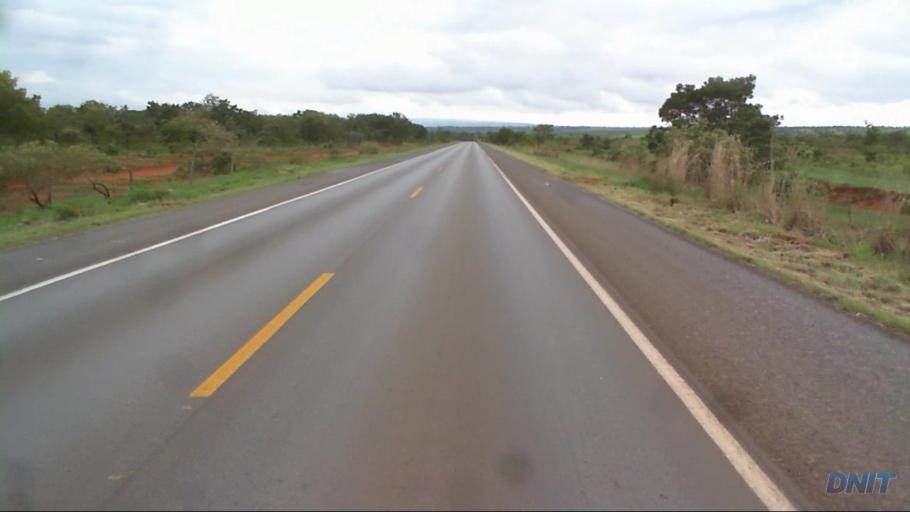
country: BR
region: Goias
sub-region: Barro Alto
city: Barro Alto
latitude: -15.2092
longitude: -48.6796
